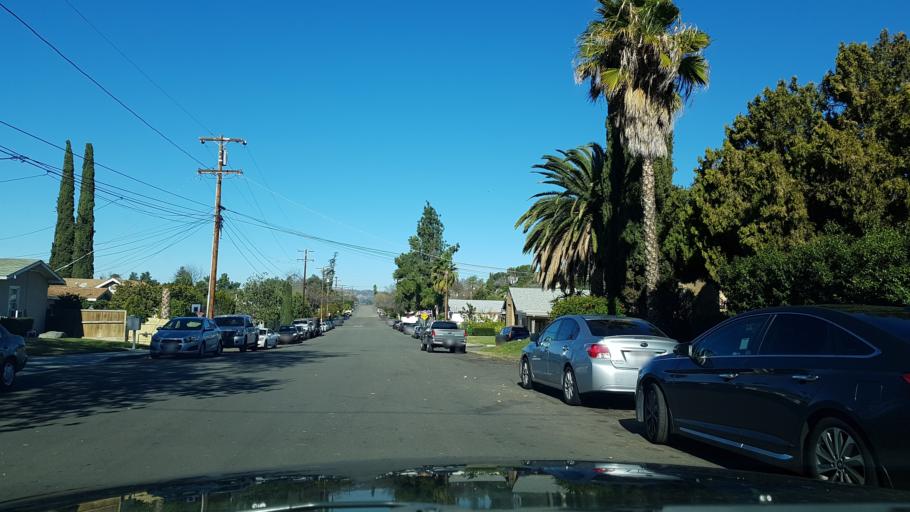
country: US
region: California
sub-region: San Diego County
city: Escondido
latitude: 33.1107
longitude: -117.0756
